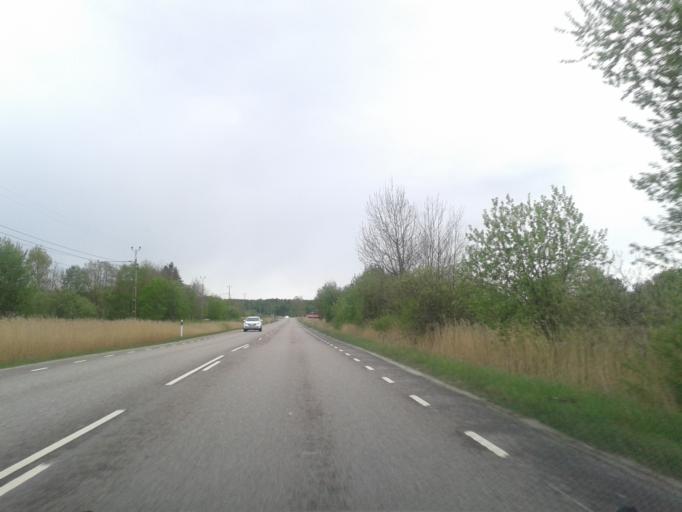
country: SE
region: Vaestra Goetaland
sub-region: Stenungsunds Kommun
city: Stora Hoga
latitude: 58.0068
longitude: 11.8295
